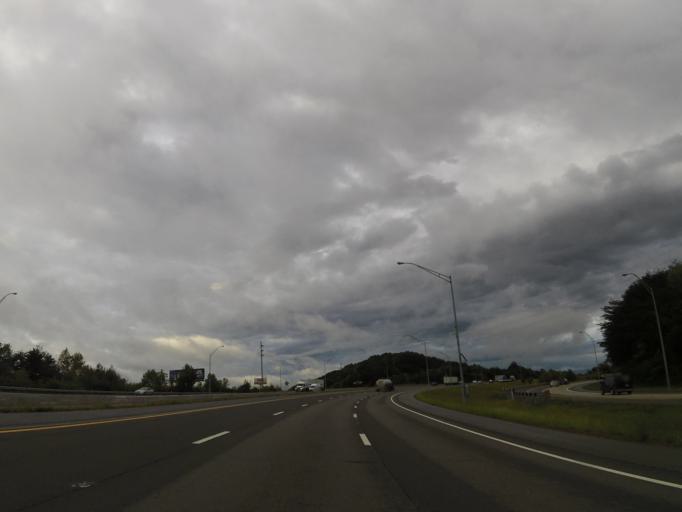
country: US
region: Tennessee
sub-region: Knox County
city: Knoxville
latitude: 36.0318
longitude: -83.8916
